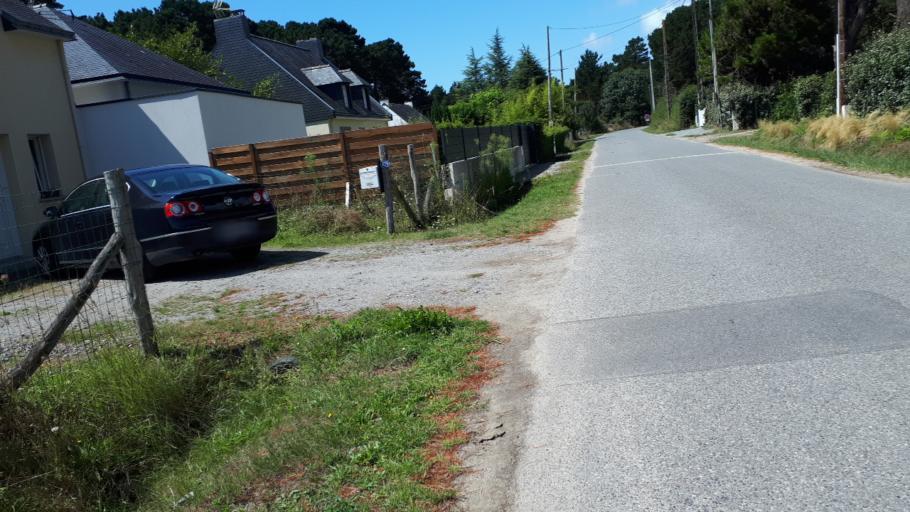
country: FR
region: Brittany
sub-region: Departement du Morbihan
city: Penestin
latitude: 47.4935
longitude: -2.4911
